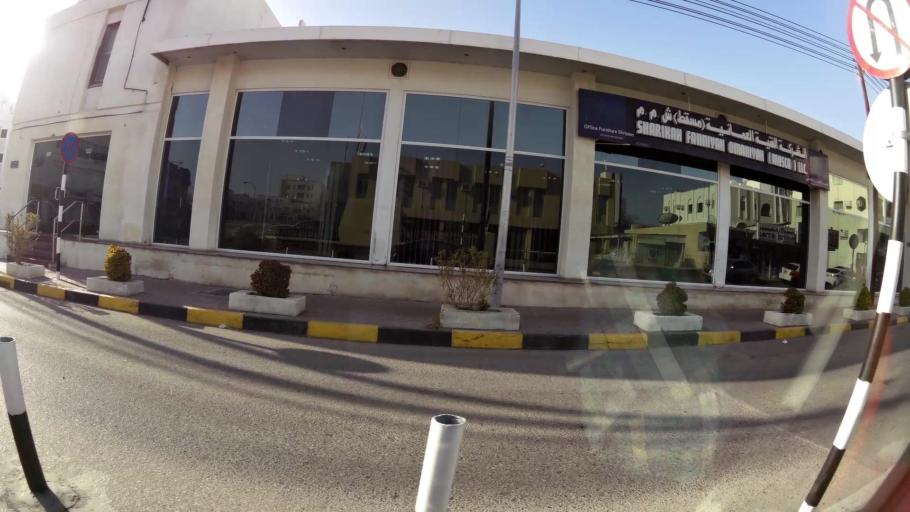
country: OM
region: Muhafazat Masqat
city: Muscat
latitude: 23.5938
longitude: 58.5451
